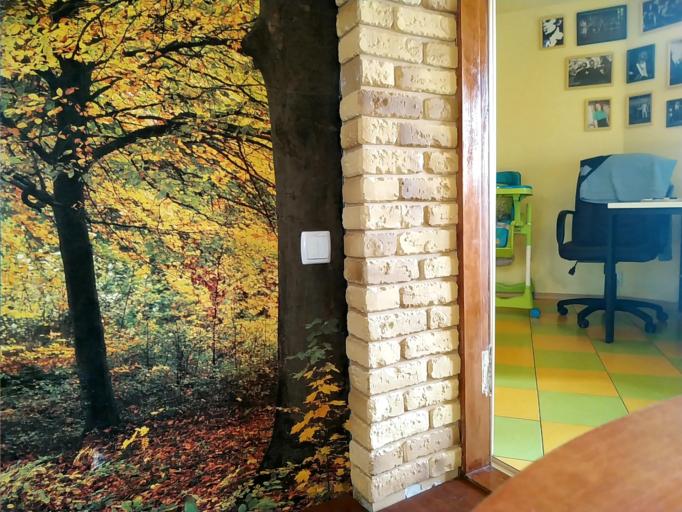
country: RU
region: Jaroslavl
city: Krasnyy Profintern
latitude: 58.0452
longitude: 40.4493
